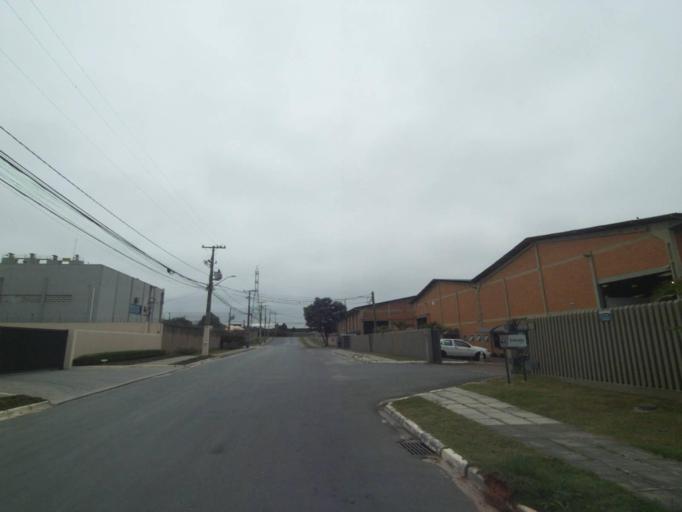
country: BR
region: Parana
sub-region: Araucaria
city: Araucaria
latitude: -25.5493
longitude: -49.3305
